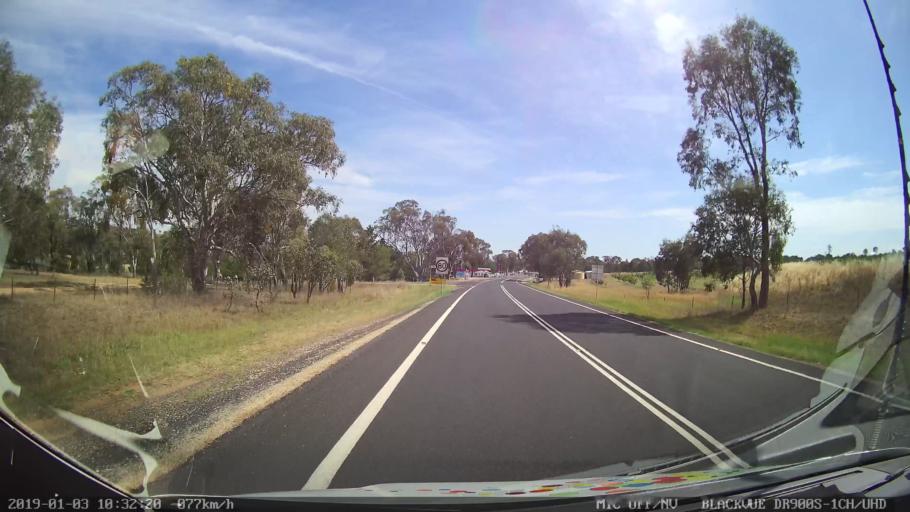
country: AU
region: New South Wales
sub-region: Young
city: Young
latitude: -34.3401
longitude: 148.2828
